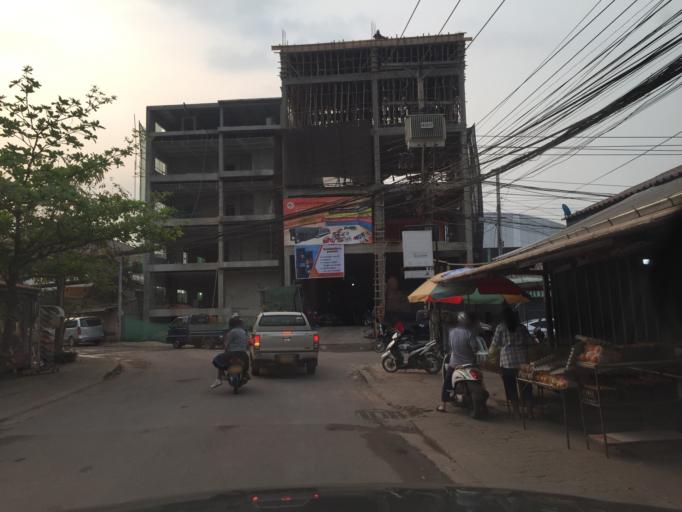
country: LA
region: Vientiane
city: Vientiane
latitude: 17.9749
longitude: 102.6101
